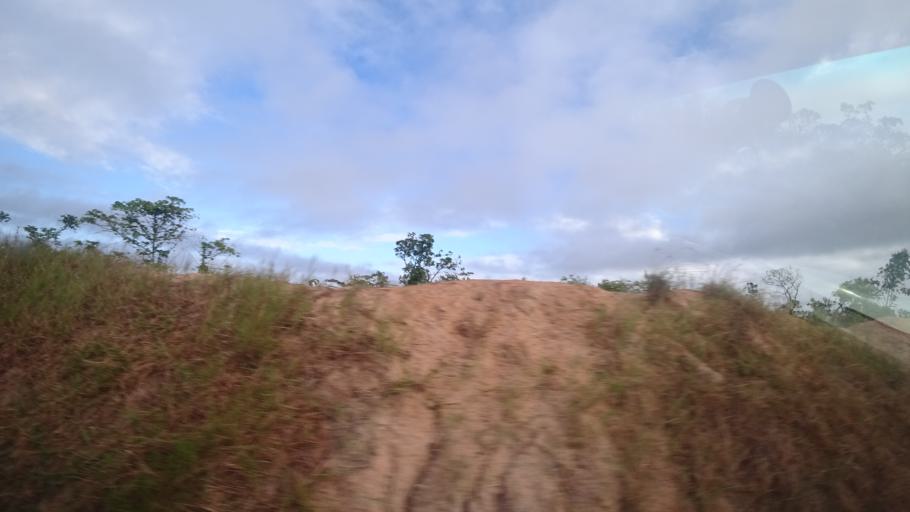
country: MZ
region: Sofala
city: Beira
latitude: -19.6173
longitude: 35.0606
